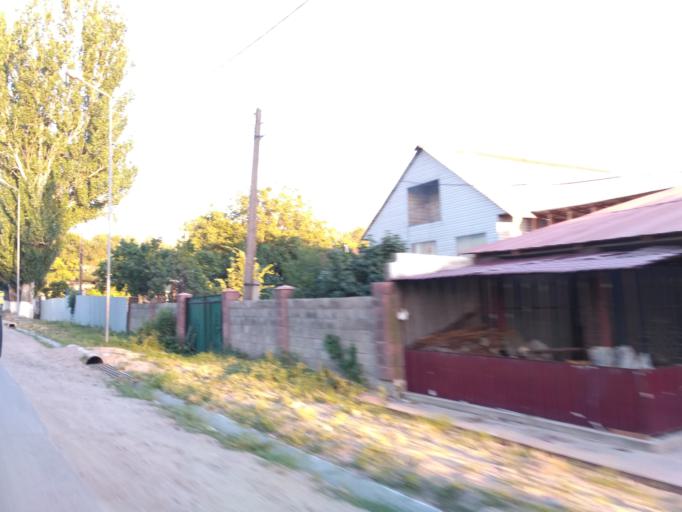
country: KZ
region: Almaty Qalasy
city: Almaty
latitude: 43.1758
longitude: 76.7606
